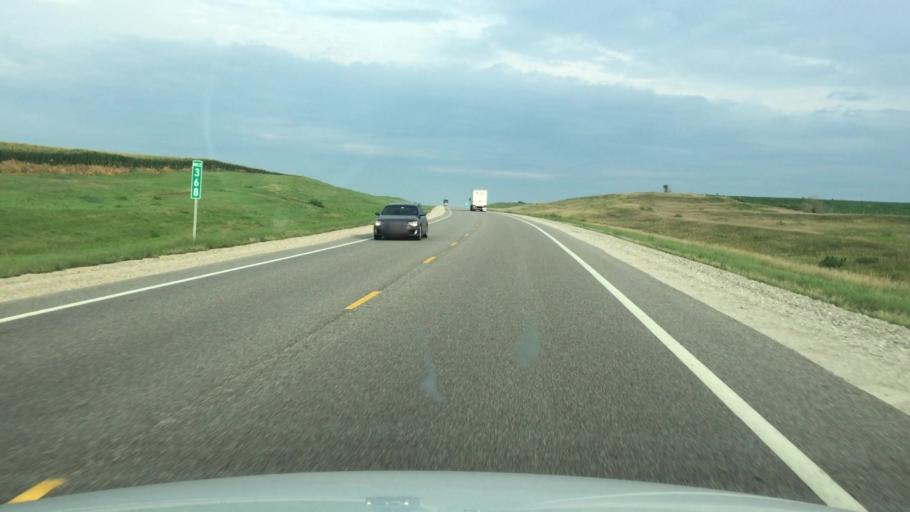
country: US
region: Kansas
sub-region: Doniphan County
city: Highland
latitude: 39.8351
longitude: -95.2383
